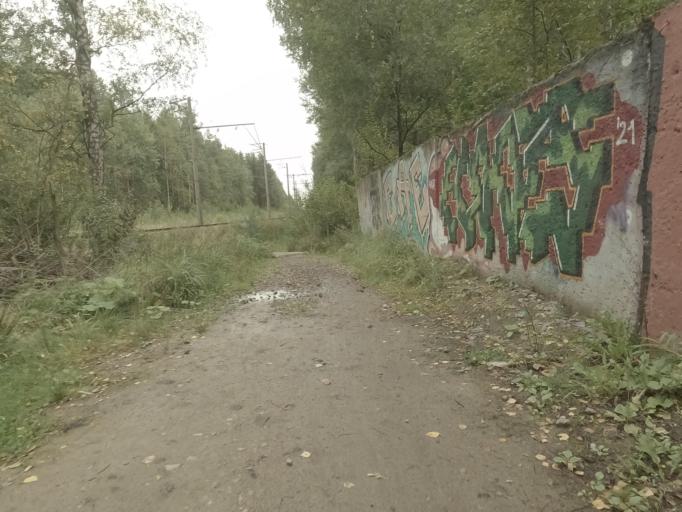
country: RU
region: St.-Petersburg
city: Krasnogvargeisky
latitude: 59.9685
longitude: 30.5126
